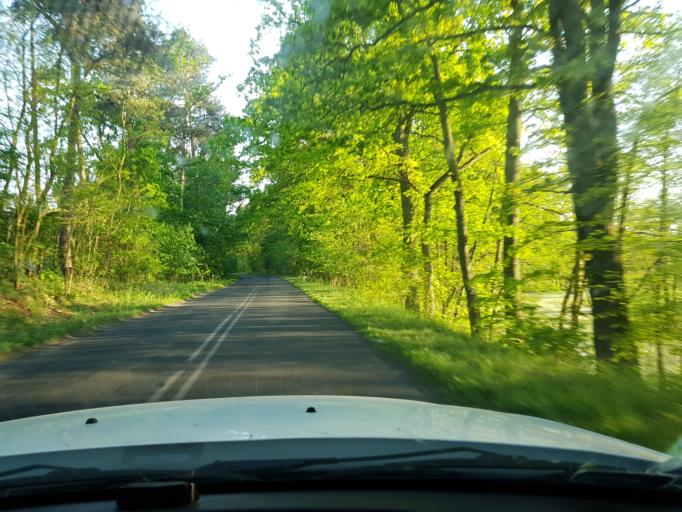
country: PL
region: West Pomeranian Voivodeship
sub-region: Powiat stargardzki
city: Kobylanka
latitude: 53.4386
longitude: 14.9098
